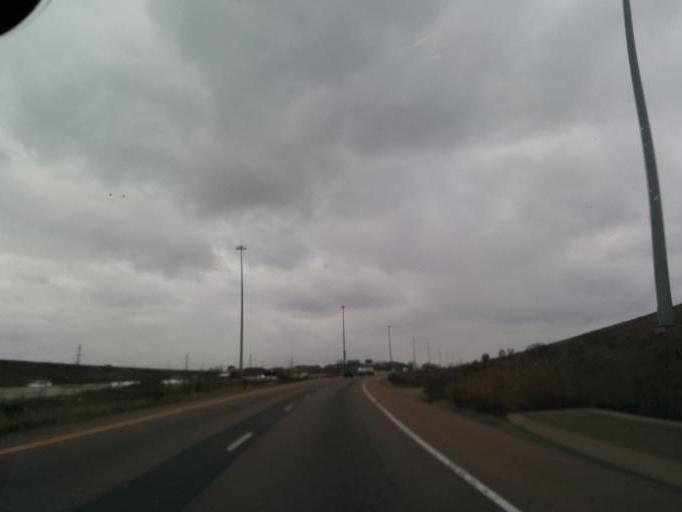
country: CA
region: Ontario
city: Mississauga
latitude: 43.6419
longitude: -79.6630
